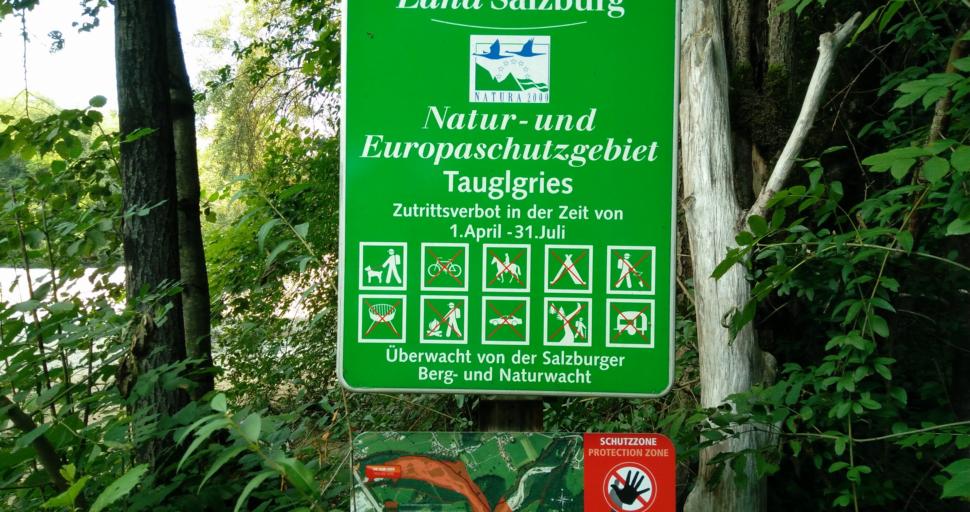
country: AT
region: Salzburg
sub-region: Politischer Bezirk Hallein
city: Adnet
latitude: 47.6584
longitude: 13.1328
